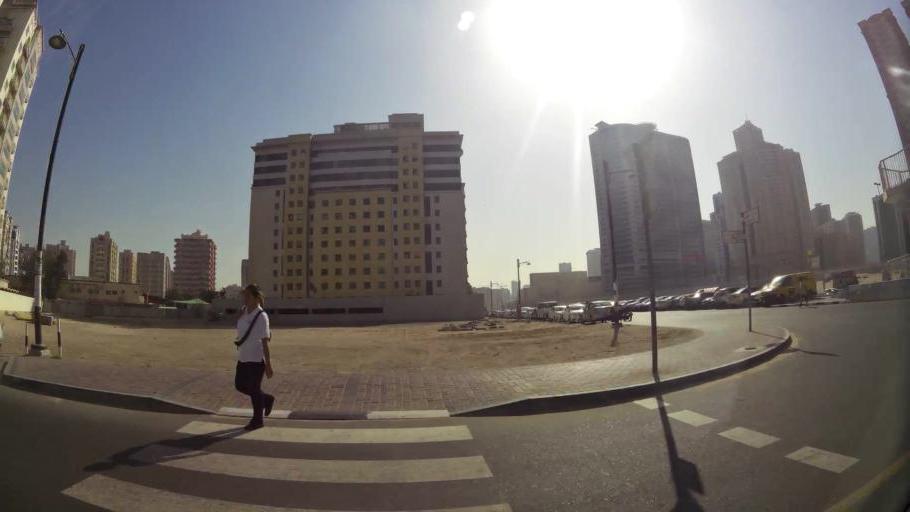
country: AE
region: Ash Shariqah
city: Sharjah
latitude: 25.2977
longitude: 55.3802
